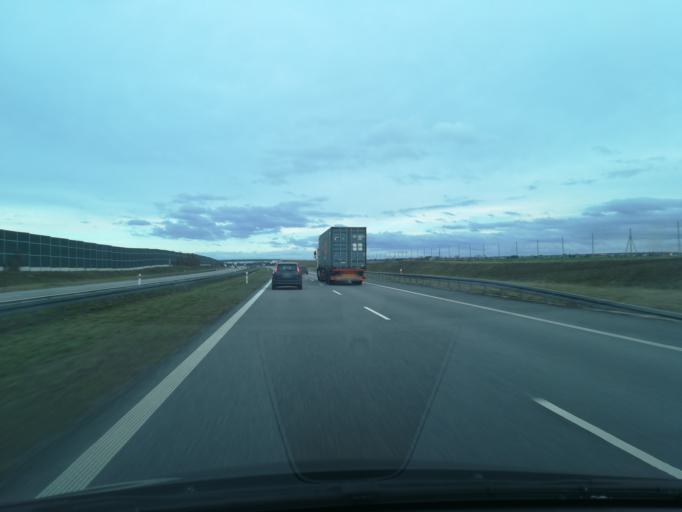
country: PL
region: Kujawsko-Pomorskie
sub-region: Powiat wloclawski
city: Czerniewice
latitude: 52.5381
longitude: 19.0593
